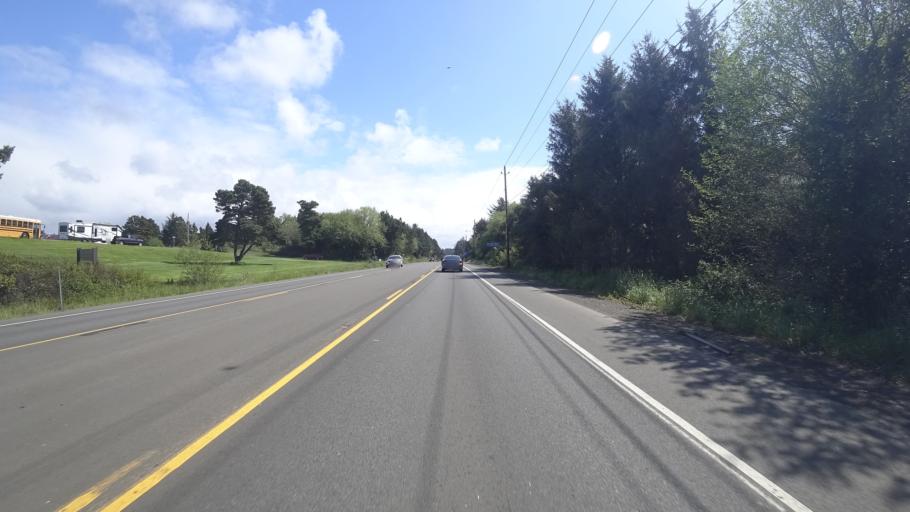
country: US
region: Oregon
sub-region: Lincoln County
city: Newport
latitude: 44.6678
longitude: -124.0573
